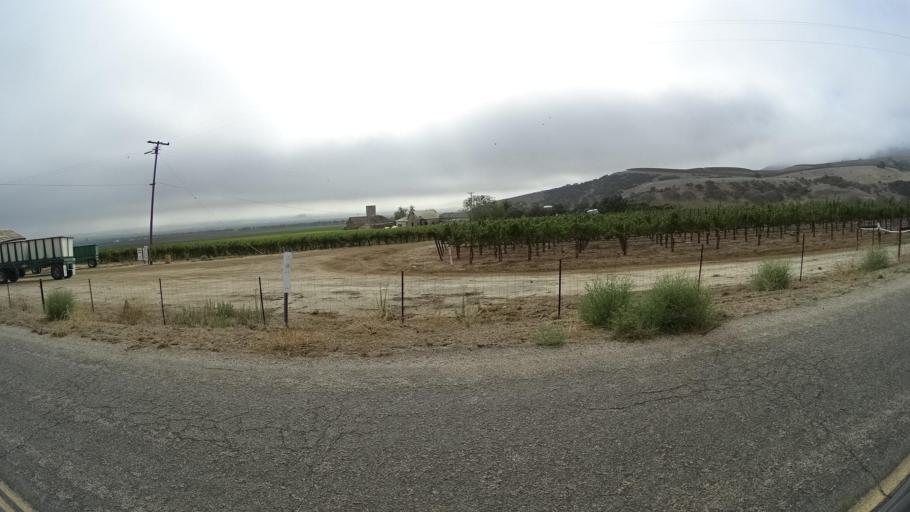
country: US
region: California
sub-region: Monterey County
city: Soledad
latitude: 36.3387
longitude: -121.3429
